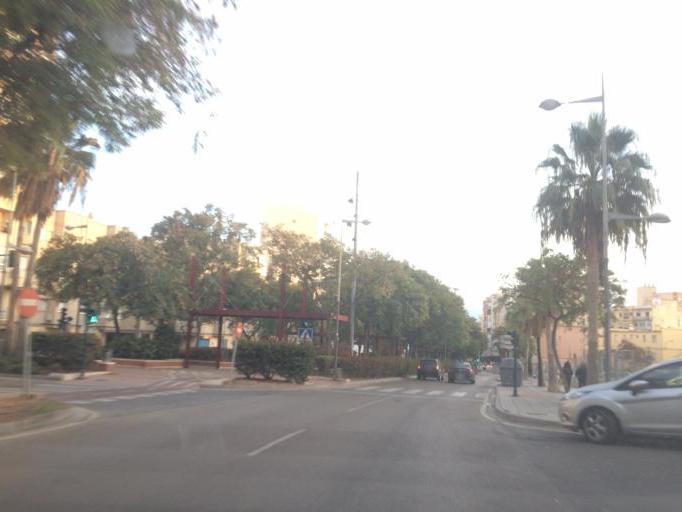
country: ES
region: Andalusia
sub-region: Provincia de Almeria
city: Almeria
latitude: 36.8475
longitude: -2.4600
